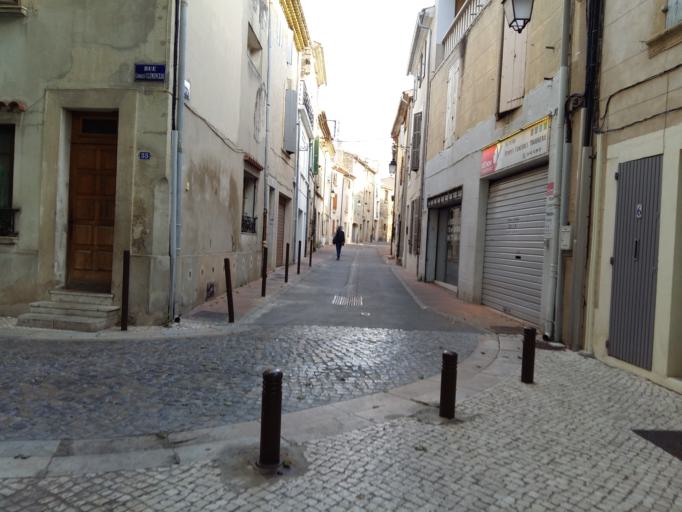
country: FR
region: Provence-Alpes-Cote d'Azur
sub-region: Departement des Bouches-du-Rhone
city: Pelissanne
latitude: 43.6312
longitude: 5.1506
